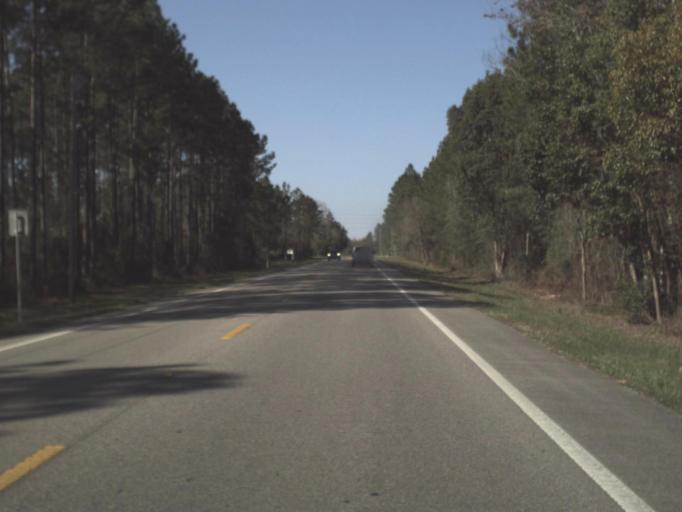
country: US
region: Florida
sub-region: Gulf County
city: Wewahitchka
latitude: 30.1946
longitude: -85.2071
